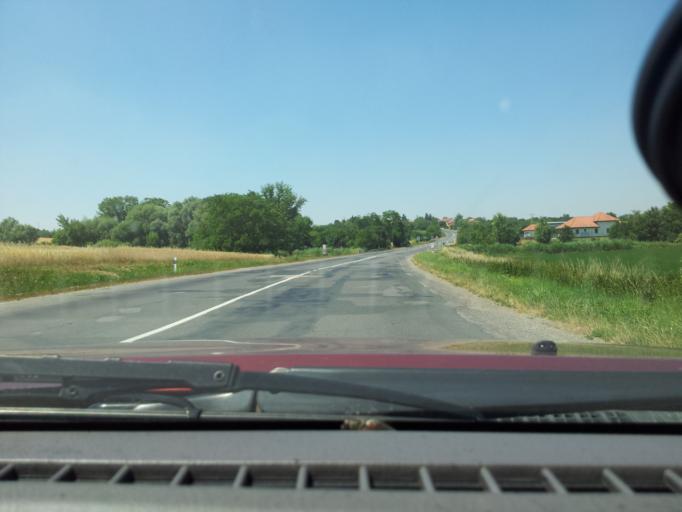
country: CZ
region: South Moravian
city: Krumvir
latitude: 48.9931
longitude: 16.8946
